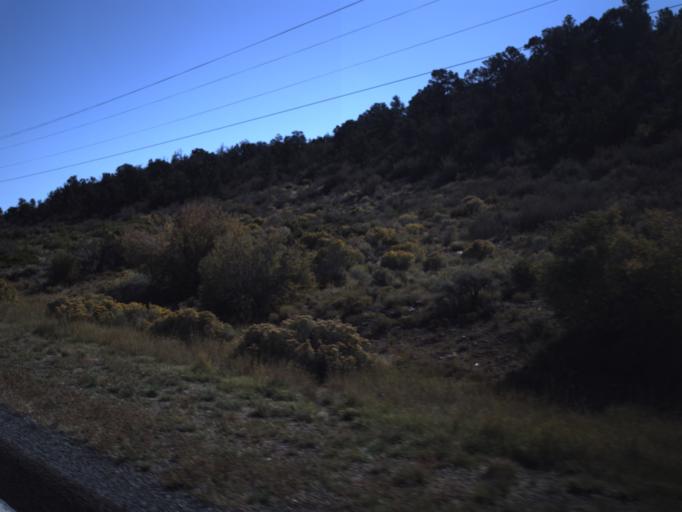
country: US
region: Utah
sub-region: Iron County
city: Cedar City
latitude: 37.6116
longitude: -113.3468
